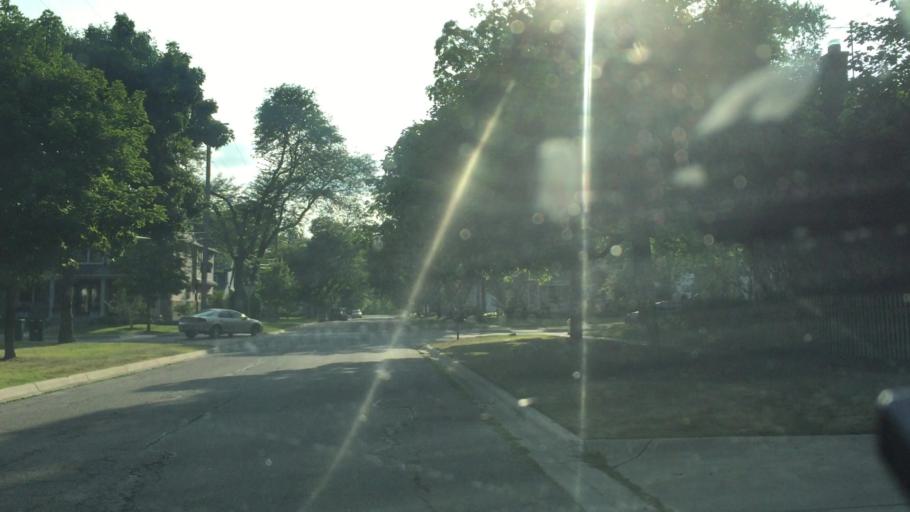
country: US
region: Michigan
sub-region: Oakland County
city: Beverly Hills
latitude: 42.5340
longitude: -83.2186
